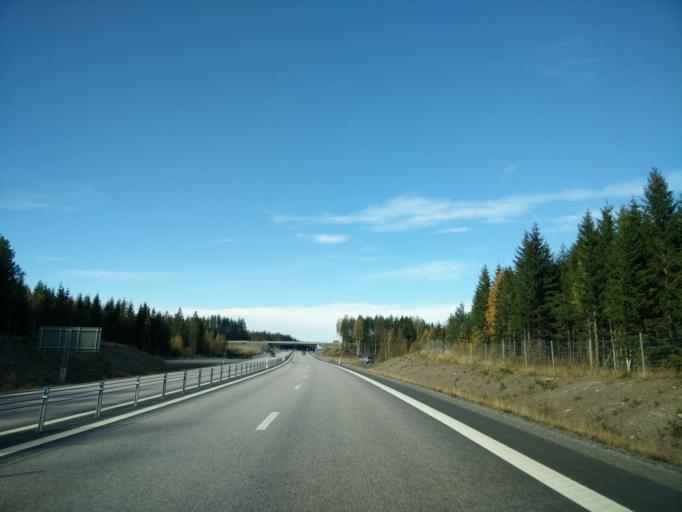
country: SE
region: Gaevleborg
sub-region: Hudiksvalls Kommun
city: Iggesund
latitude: 61.5483
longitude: 16.9790
